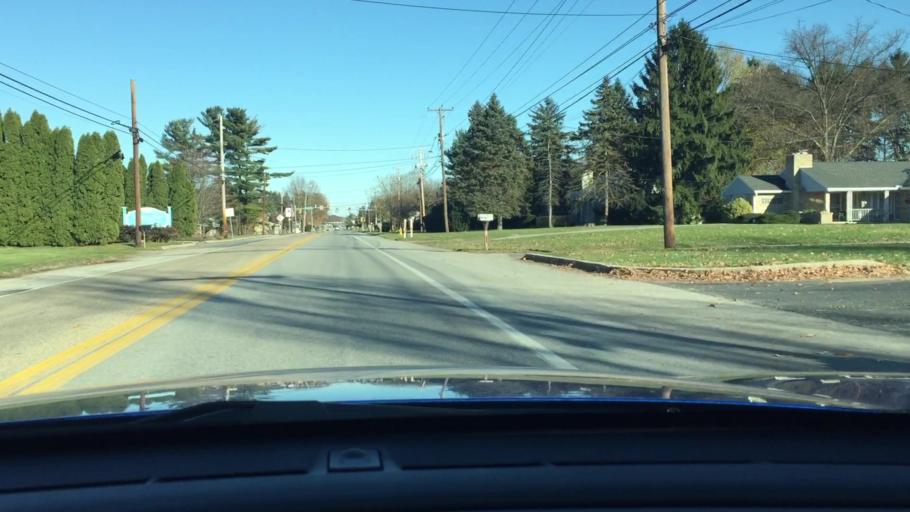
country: US
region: Pennsylvania
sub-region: Cumberland County
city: Shiremanstown
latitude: 40.2273
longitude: -76.9664
